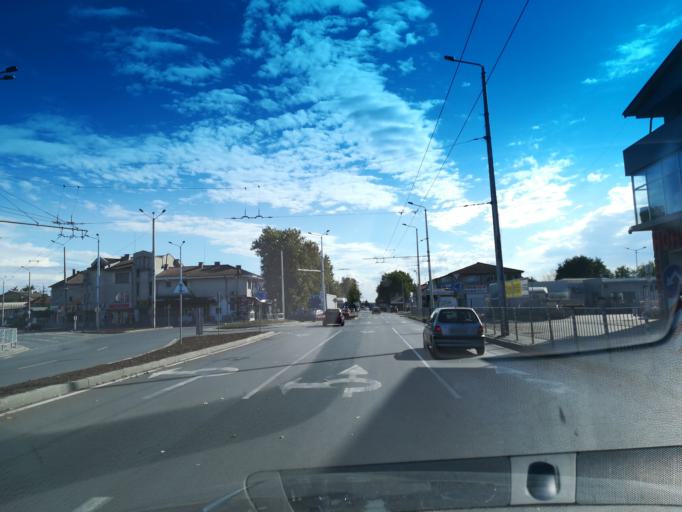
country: BG
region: Stara Zagora
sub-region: Obshtina Stara Zagora
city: Stara Zagora
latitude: 42.3991
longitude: 25.6442
